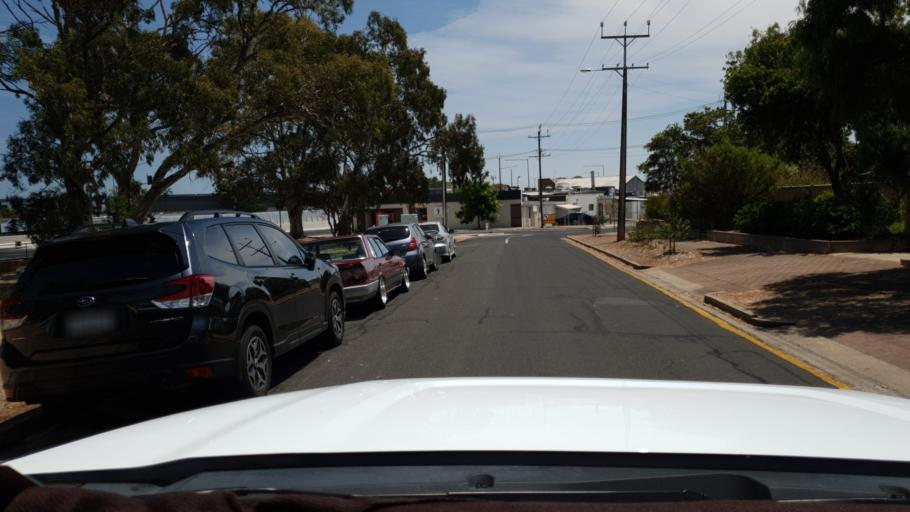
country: AU
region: South Australia
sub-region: Marion
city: Clovelly Park
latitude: -35.0083
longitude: 138.5768
